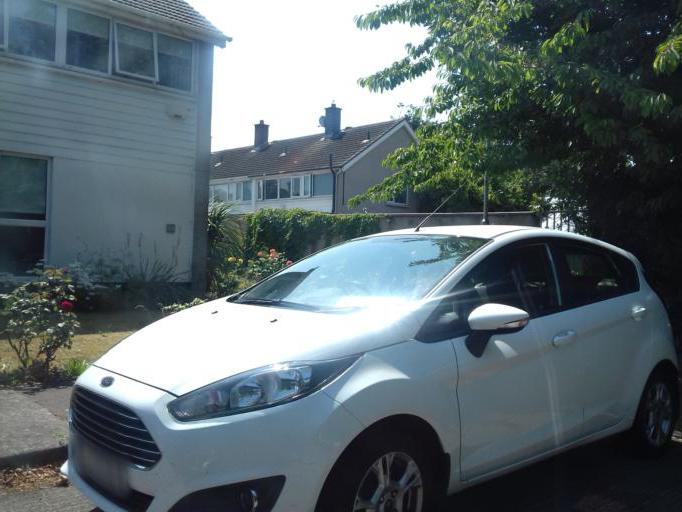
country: IE
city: Bayside
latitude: 53.3880
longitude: -6.1386
